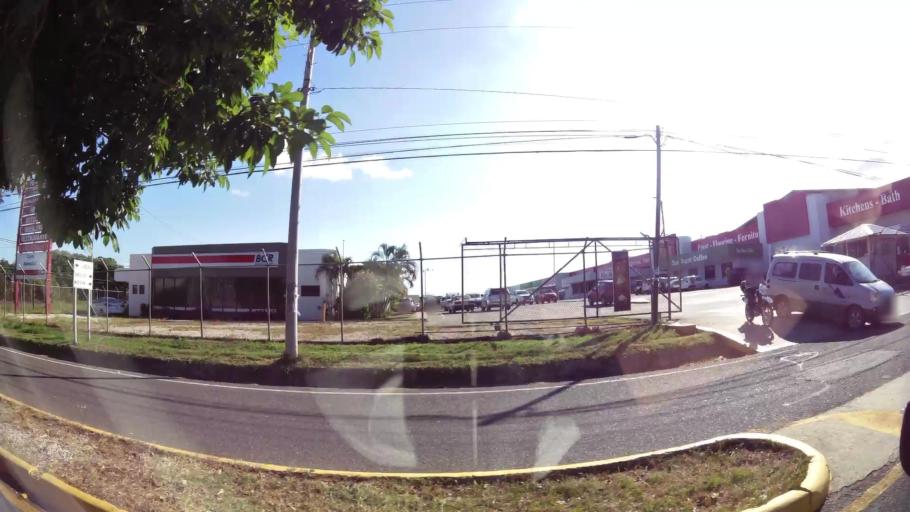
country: CR
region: Guanacaste
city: Sardinal
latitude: 10.5577
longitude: -85.5923
